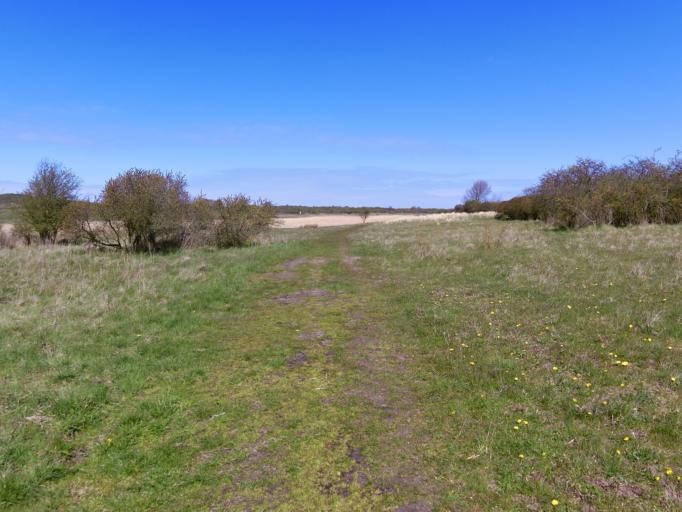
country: DE
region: Mecklenburg-Vorpommern
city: Hiddensee
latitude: 54.5970
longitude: 13.1419
